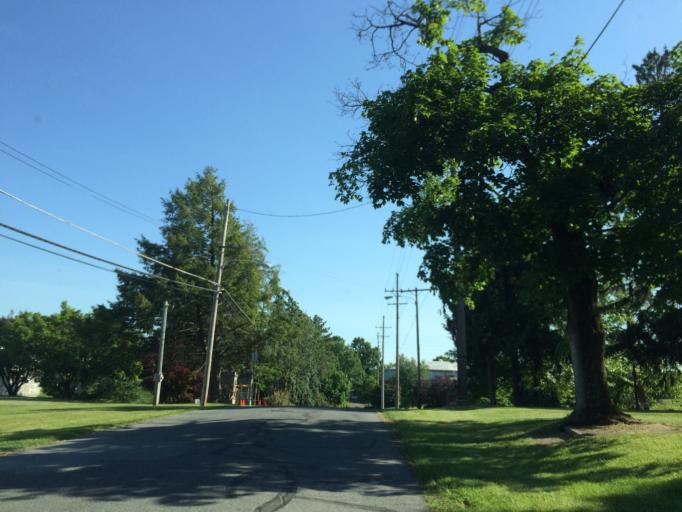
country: US
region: Maryland
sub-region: Frederick County
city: Frederick
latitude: 39.4120
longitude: -77.4401
